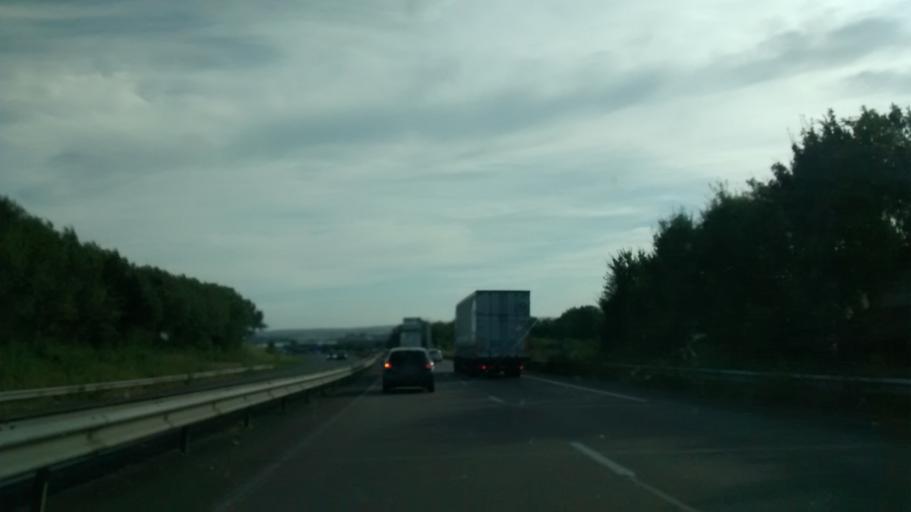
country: FR
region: Lower Normandy
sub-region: Departement du Calvados
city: Villers-Bocage
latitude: 49.0905
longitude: -0.6329
